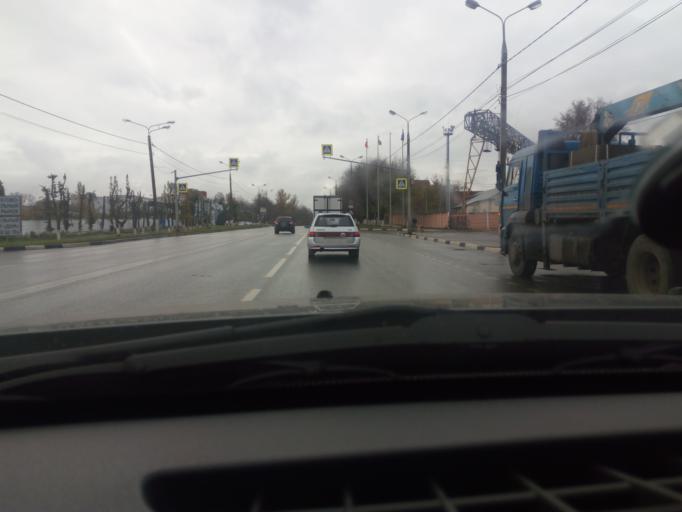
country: RU
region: Moskovskaya
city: Domodedovo
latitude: 55.4460
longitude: 37.7646
